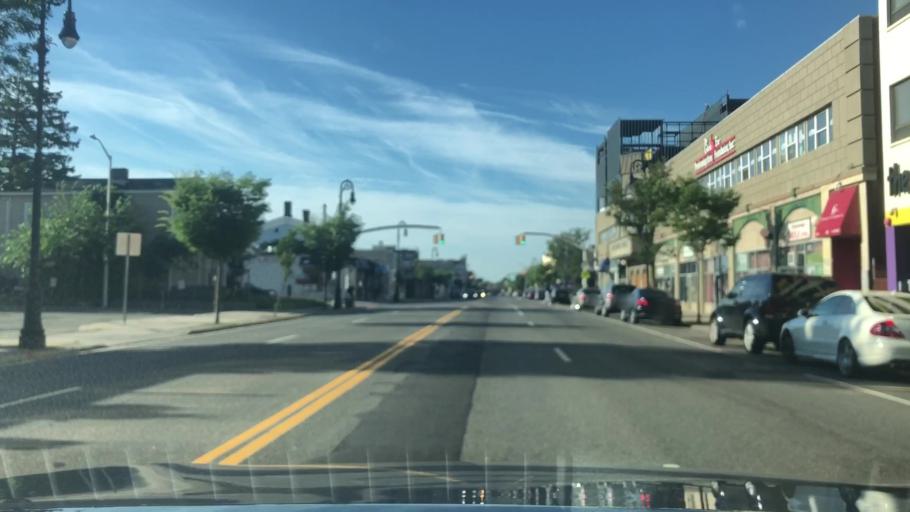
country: US
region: New York
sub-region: Nassau County
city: Hempstead
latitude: 40.7114
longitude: -73.6285
